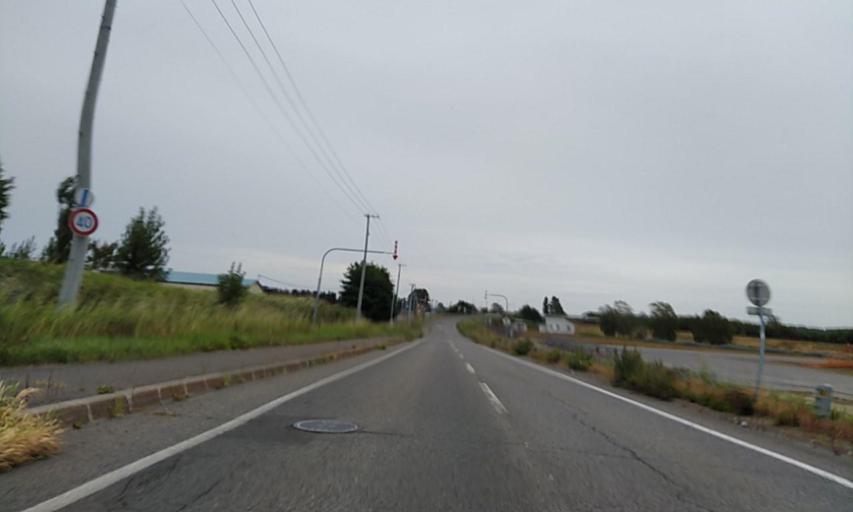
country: JP
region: Hokkaido
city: Bihoro
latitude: 43.8358
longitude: 144.1105
